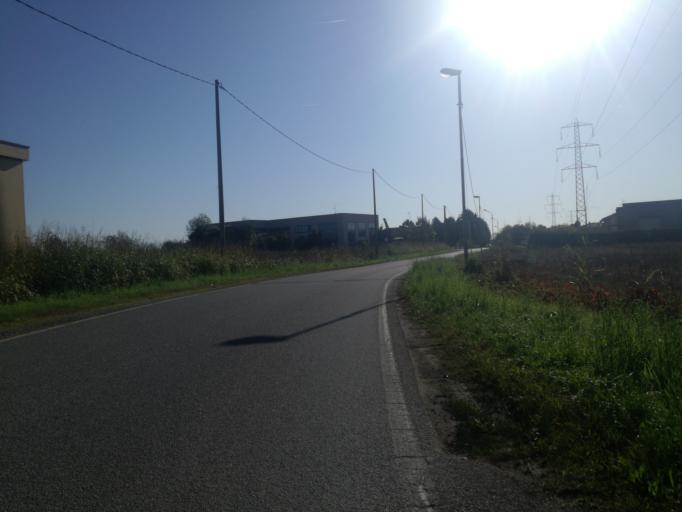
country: IT
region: Lombardy
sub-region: Provincia di Monza e Brianza
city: Porto d'Adda
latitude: 45.6490
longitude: 9.4762
